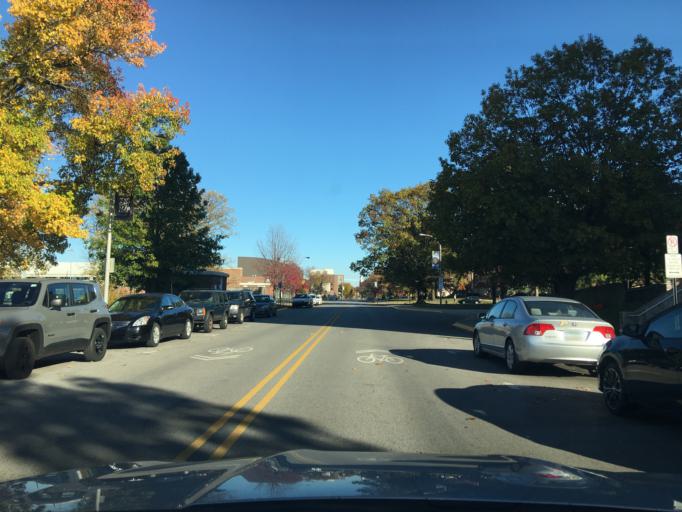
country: US
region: Indiana
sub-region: Tippecanoe County
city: West Lafayette
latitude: 40.4274
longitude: -86.9271
